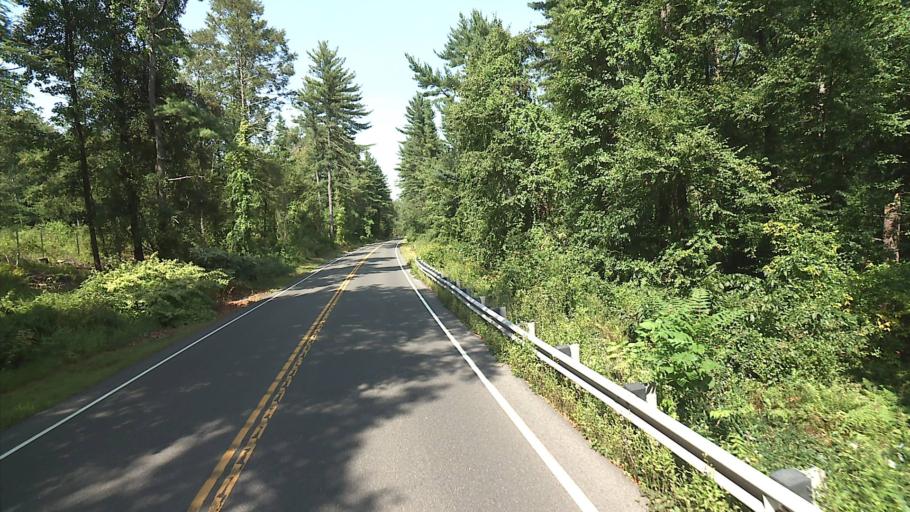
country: US
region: Connecticut
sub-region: Fairfield County
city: Fairfield
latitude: 41.2117
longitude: -73.2894
